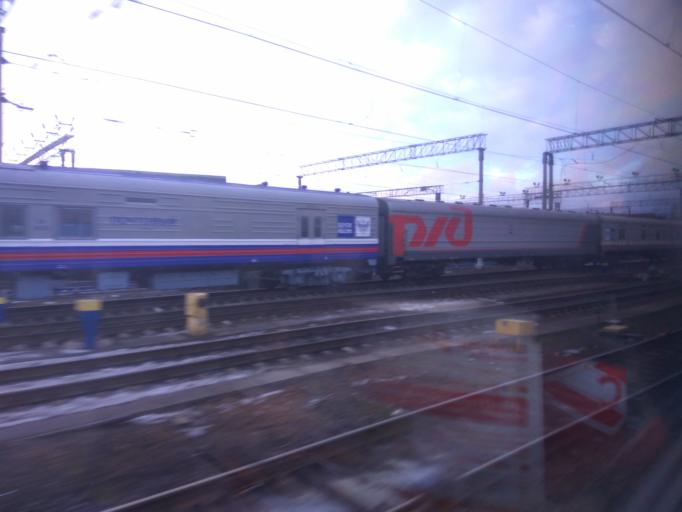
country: RU
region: St.-Petersburg
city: Centralniy
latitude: 59.9196
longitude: 30.3663
